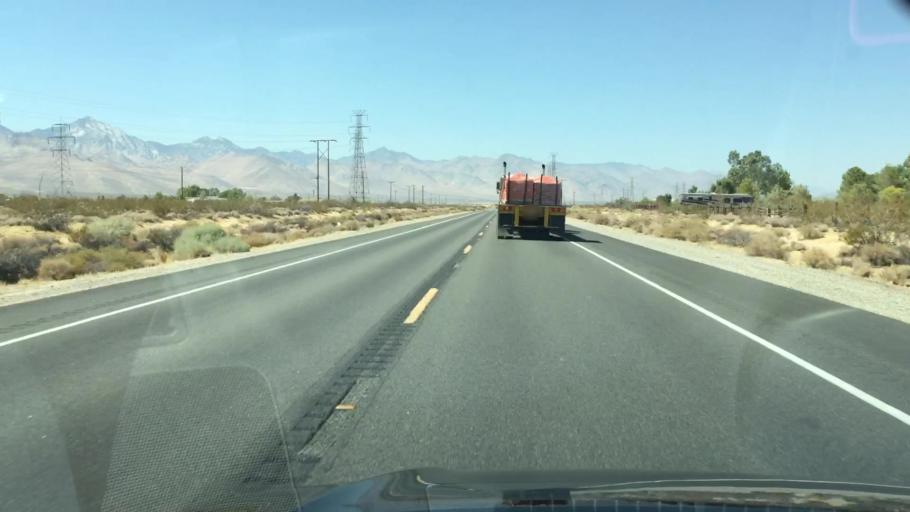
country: US
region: California
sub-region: Kern County
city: China Lake Acres
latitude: 35.6375
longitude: -117.7885
